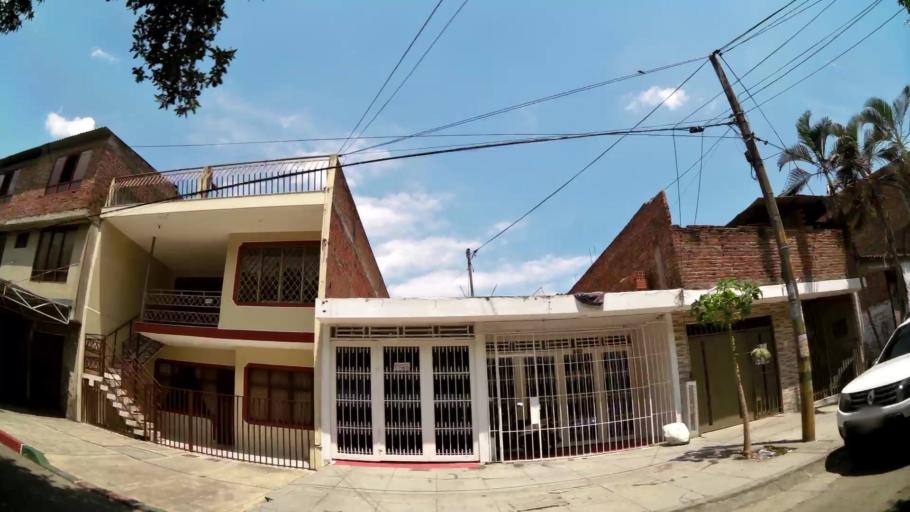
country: CO
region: Valle del Cauca
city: Cali
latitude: 3.4488
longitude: -76.5102
